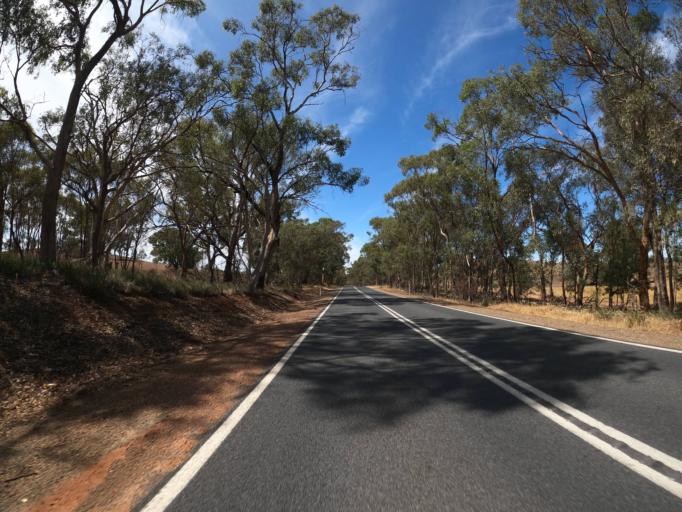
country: AU
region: Victoria
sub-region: Benalla
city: Benalla
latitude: -36.3776
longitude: 145.9756
